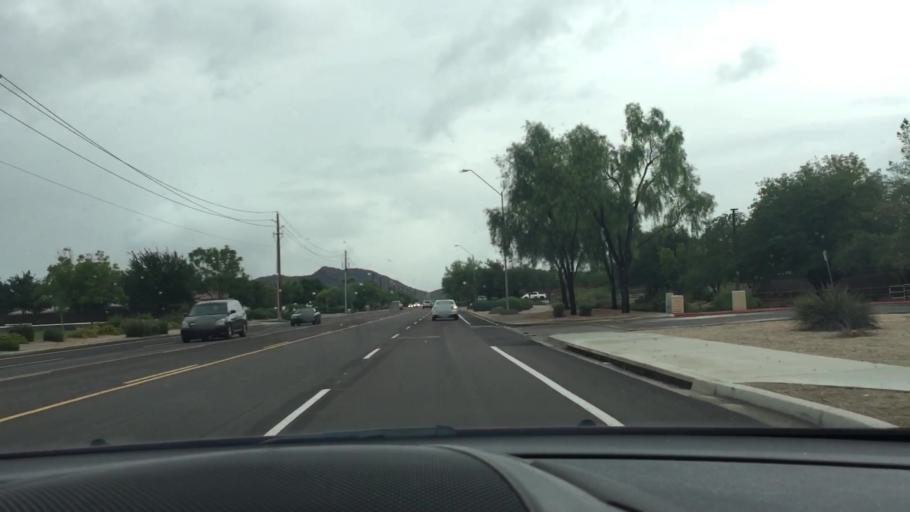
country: US
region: Arizona
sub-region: Maricopa County
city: Sun City
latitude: 33.6834
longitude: -112.2377
